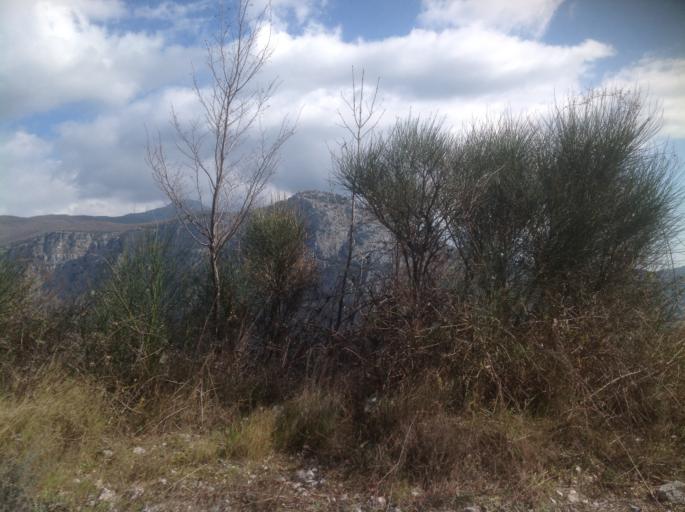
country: IT
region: Calabria
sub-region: Provincia di Cosenza
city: Civita
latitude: 39.8297
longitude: 16.3036
